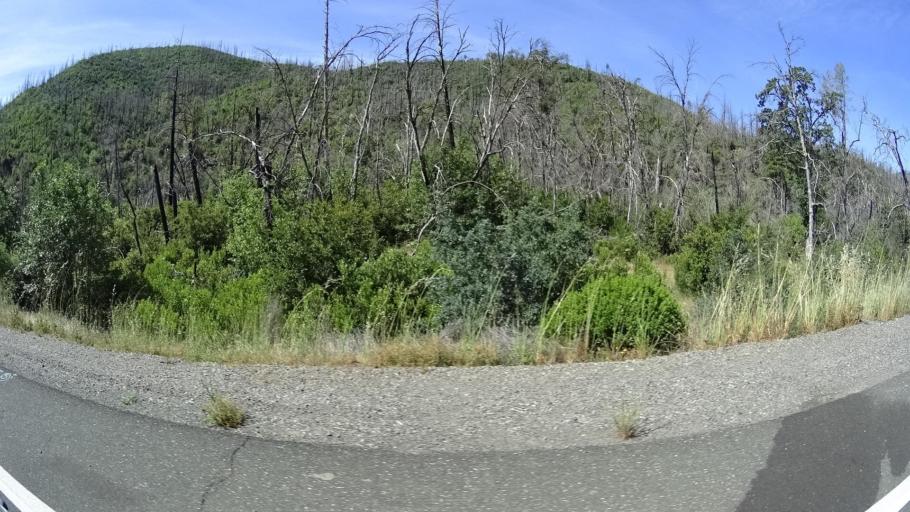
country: US
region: California
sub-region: Lake County
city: Middletown
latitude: 38.7755
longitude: -122.6751
